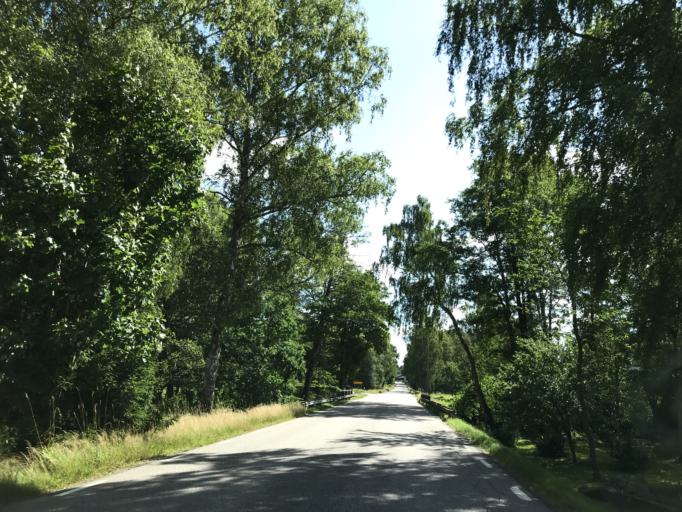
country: SE
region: Halland
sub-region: Laholms Kommun
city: Knared
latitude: 56.5213
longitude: 13.3337
